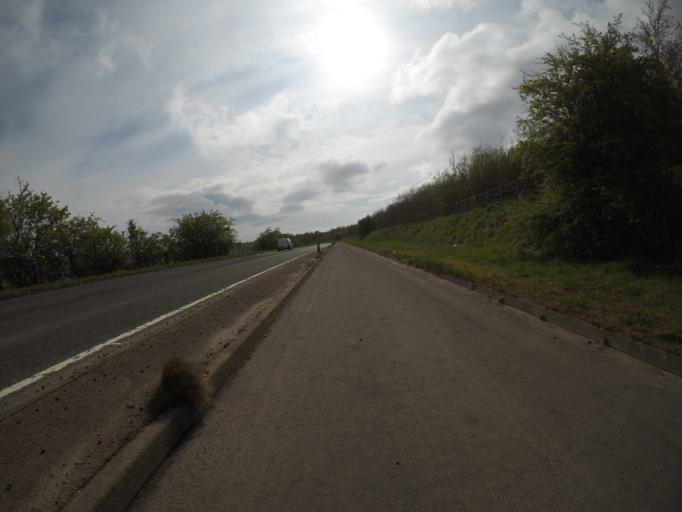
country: GB
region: Scotland
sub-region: East Renfrewshire
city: Newton Mearns
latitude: 55.7399
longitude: -4.3742
